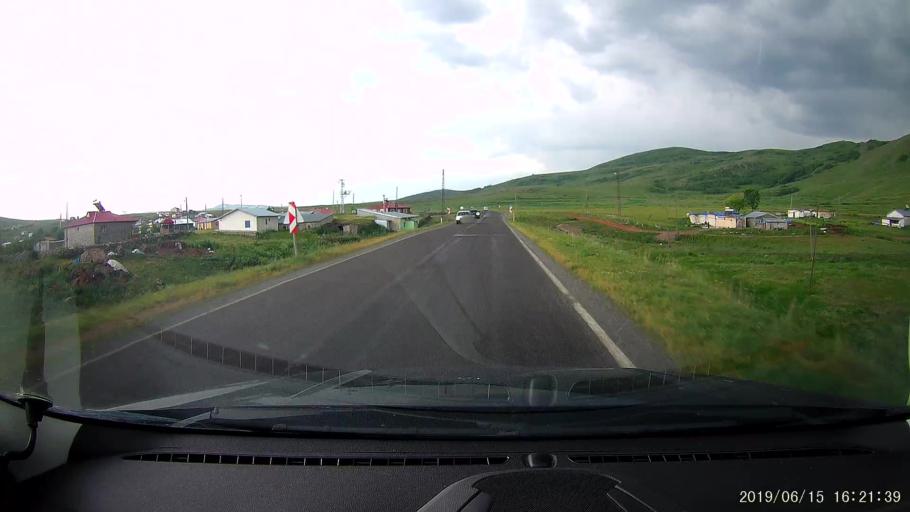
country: TR
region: Ardahan
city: Hanak
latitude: 41.1971
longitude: 42.8468
